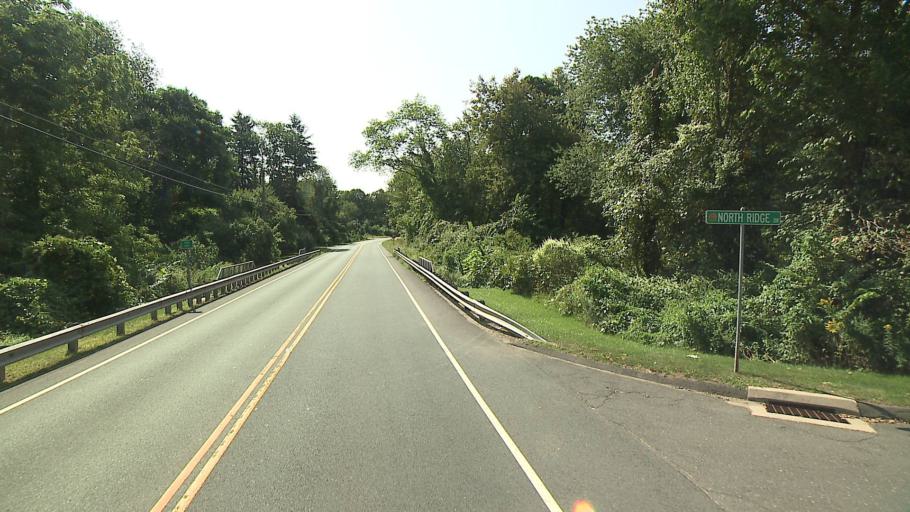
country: US
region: Connecticut
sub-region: Fairfield County
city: Newtown
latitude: 41.4325
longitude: -73.3549
